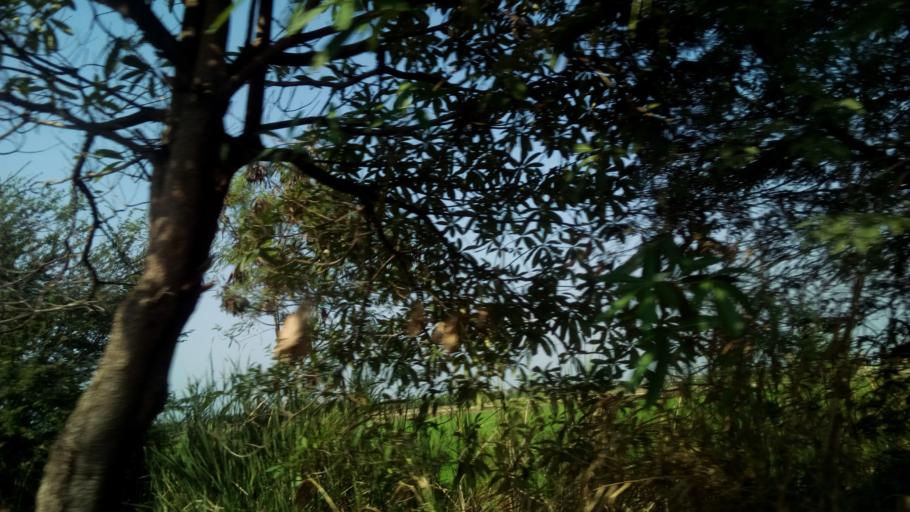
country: TH
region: Nonthaburi
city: Sai Noi
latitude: 13.9374
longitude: 100.3389
